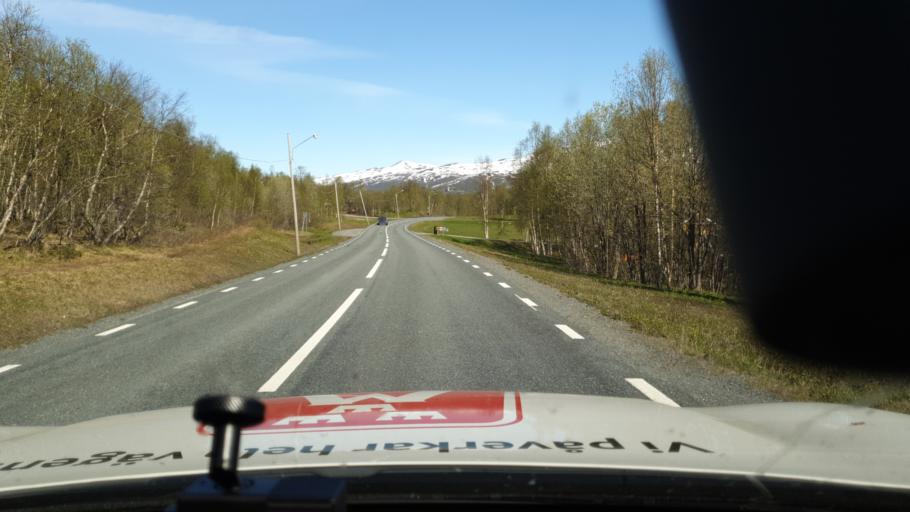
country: NO
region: Nordland
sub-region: Rana
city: Mo i Rana
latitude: 65.7753
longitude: 15.1128
